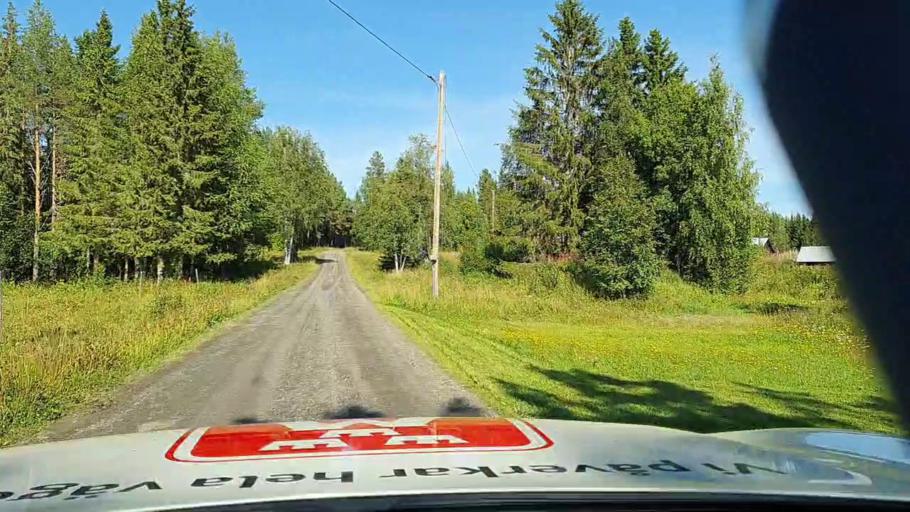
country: SE
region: Jaemtland
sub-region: Krokoms Kommun
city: Krokom
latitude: 63.7728
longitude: 14.6435
